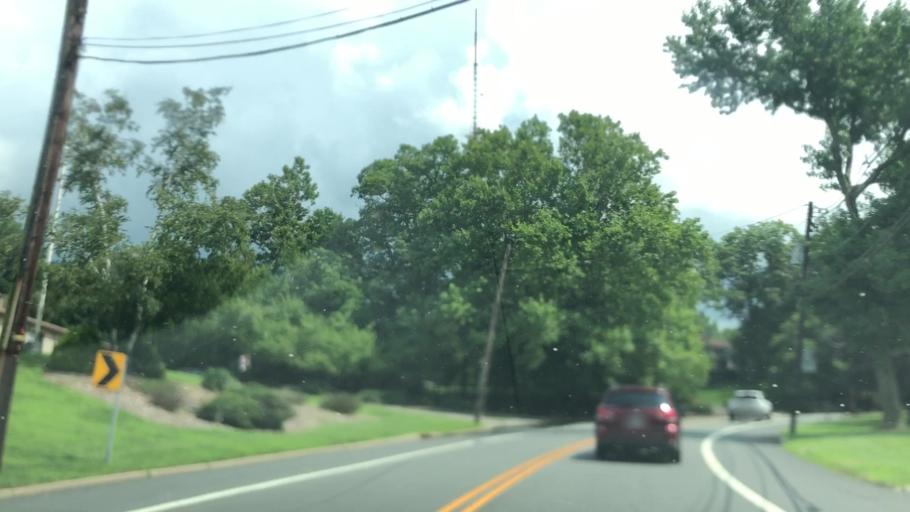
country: US
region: New Jersey
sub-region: Passaic County
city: Little Falls
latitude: 40.8663
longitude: -74.2038
